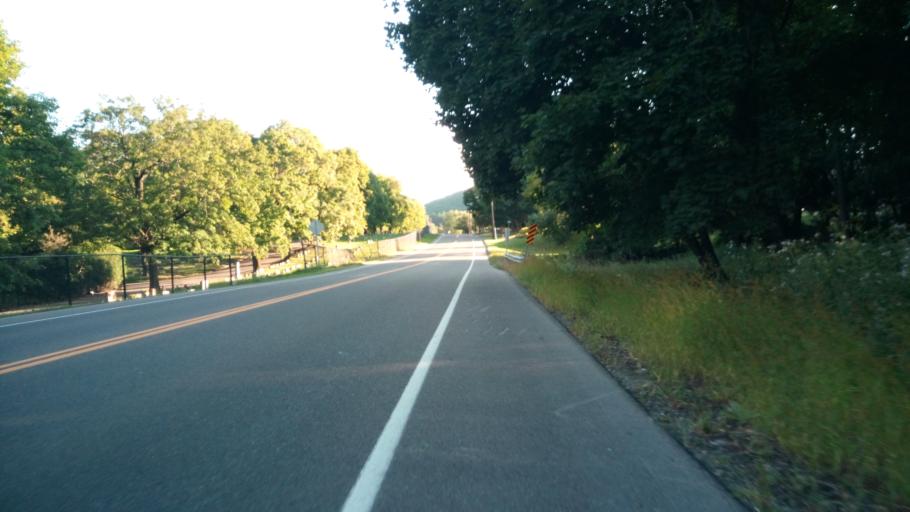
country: US
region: New York
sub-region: Chemung County
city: Elmira Heights
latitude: 42.1090
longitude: -76.8314
